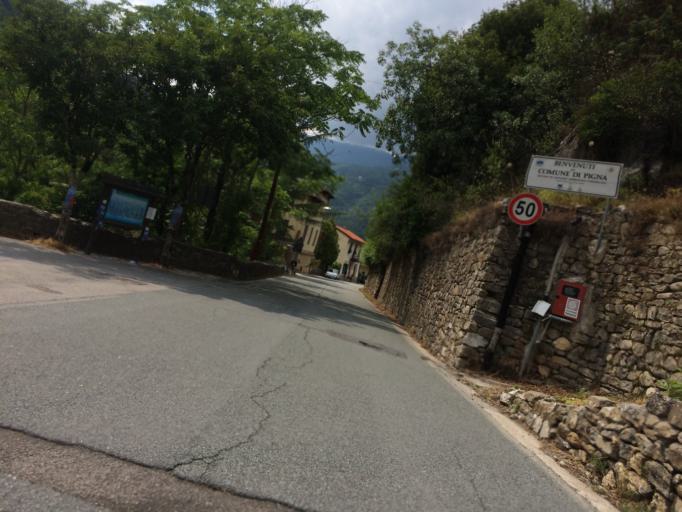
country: IT
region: Liguria
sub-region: Provincia di Imperia
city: Castel Vittorio
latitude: 43.9309
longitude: 7.6696
